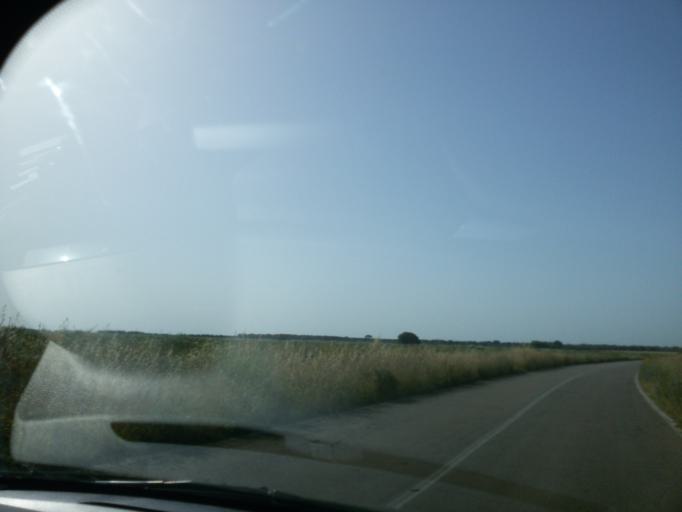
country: IT
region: Apulia
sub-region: Provincia di Brindisi
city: Mesagne
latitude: 40.5271
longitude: 17.8206
